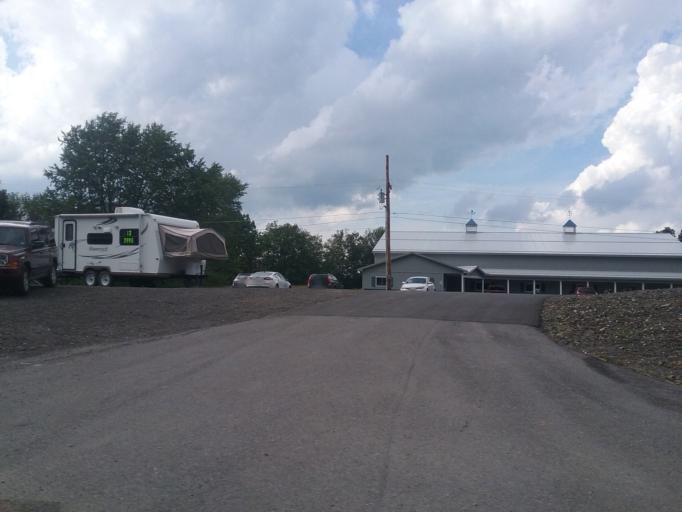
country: US
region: Pennsylvania
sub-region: Tioga County
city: Wellsboro
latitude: 41.7488
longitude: -77.2445
